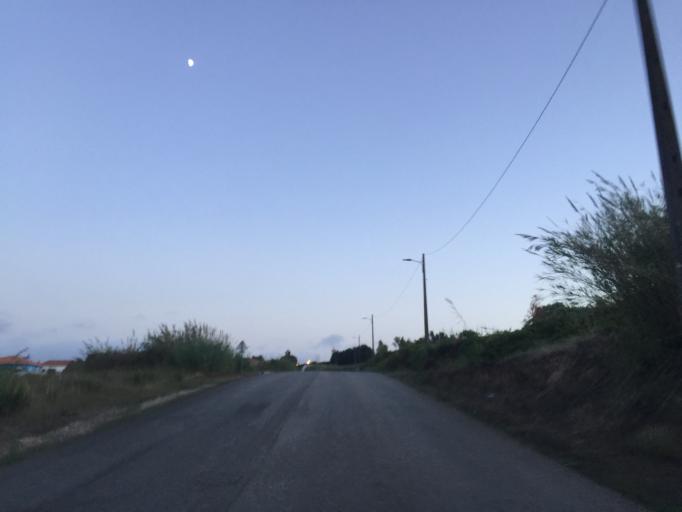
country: PT
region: Leiria
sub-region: Bombarral
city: Bombarral
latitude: 39.2729
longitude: -9.1657
